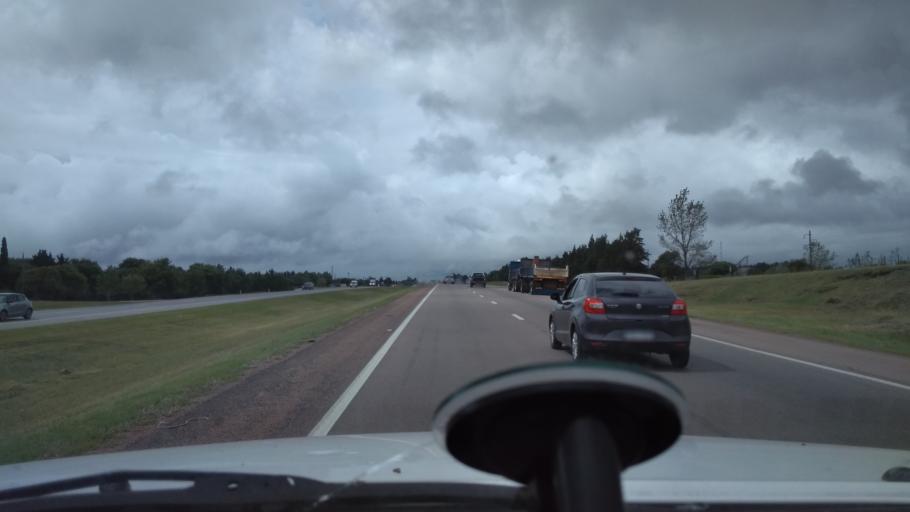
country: UY
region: Canelones
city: La Paz
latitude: -34.7418
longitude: -56.2517
